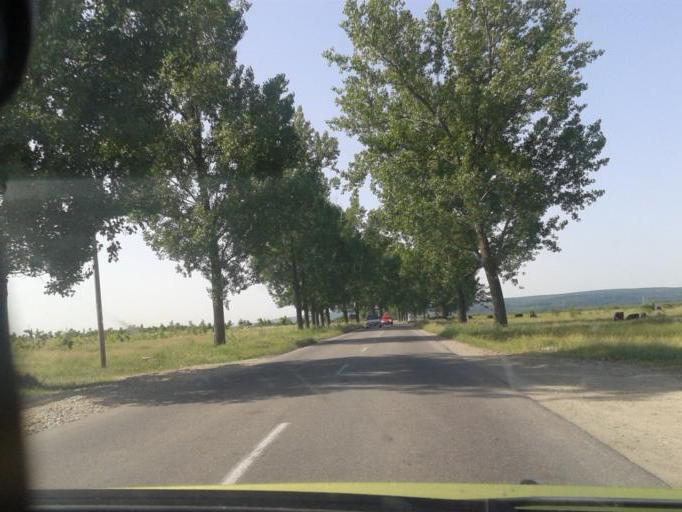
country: RO
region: Prahova
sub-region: Comuna Dumbravesti
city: Dumbravesti
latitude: 45.0773
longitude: 25.9933
